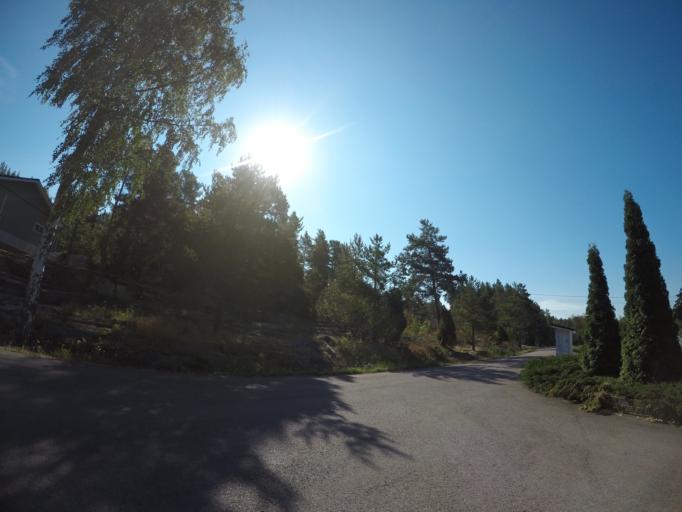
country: AX
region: Alands landsbygd
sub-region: Finstroem
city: Finstroem
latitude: 60.3339
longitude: 19.9107
